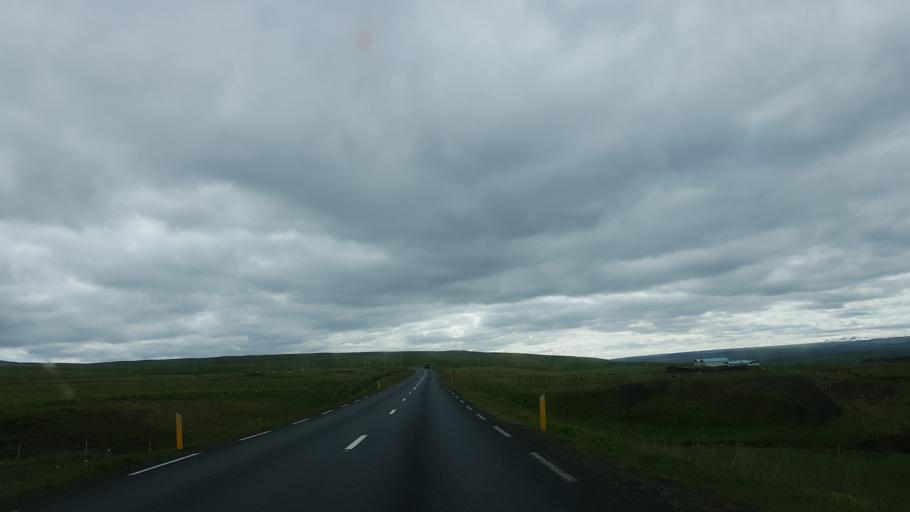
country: IS
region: Northwest
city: Saudarkrokur
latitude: 65.3574
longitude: -20.8891
